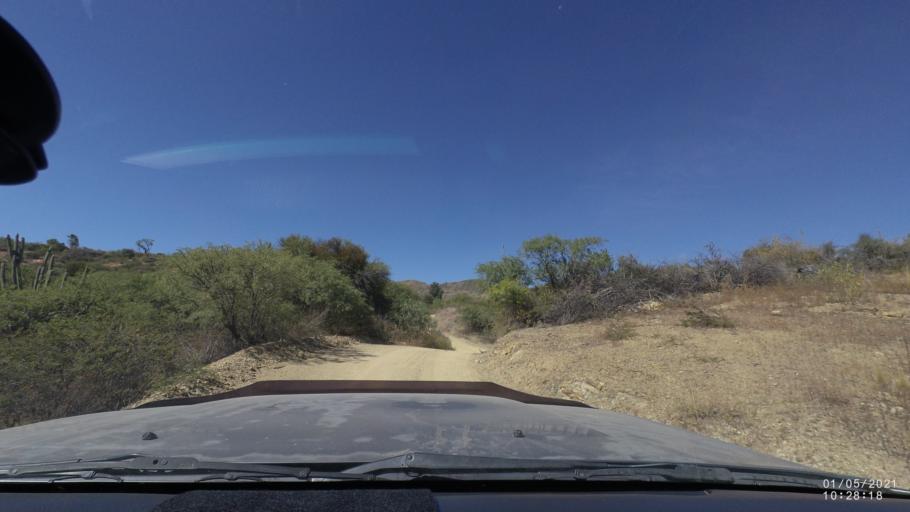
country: BO
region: Cochabamba
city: Capinota
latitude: -17.5888
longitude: -66.1897
